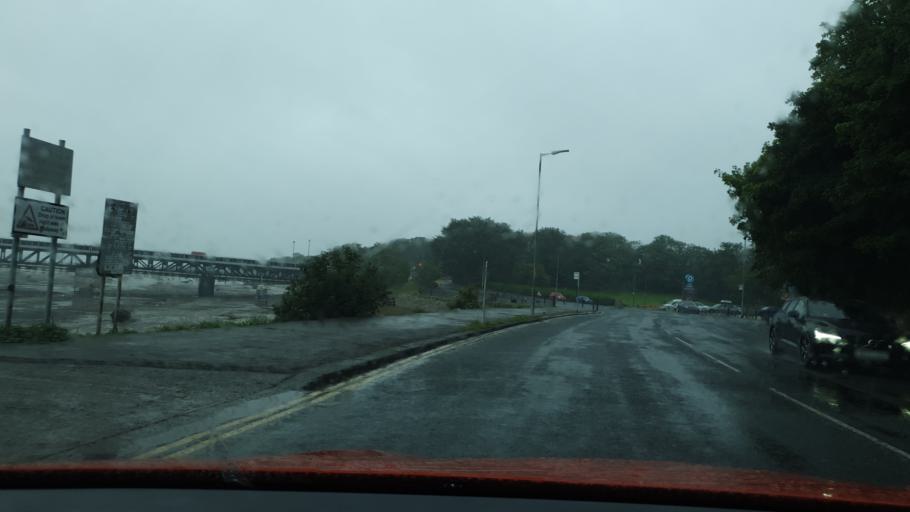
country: GB
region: England
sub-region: Cumbria
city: Barrow in Furness
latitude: 54.1091
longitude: -3.2459
